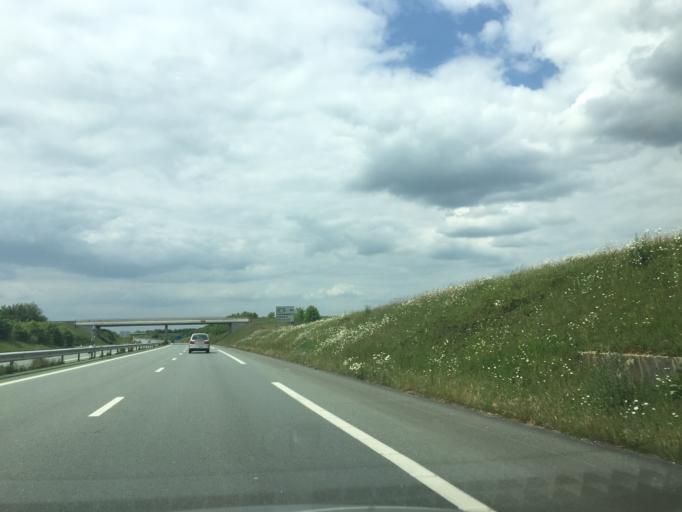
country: FR
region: Poitou-Charentes
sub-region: Departement des Deux-Sevres
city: Echire
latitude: 46.4186
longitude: -0.4077
